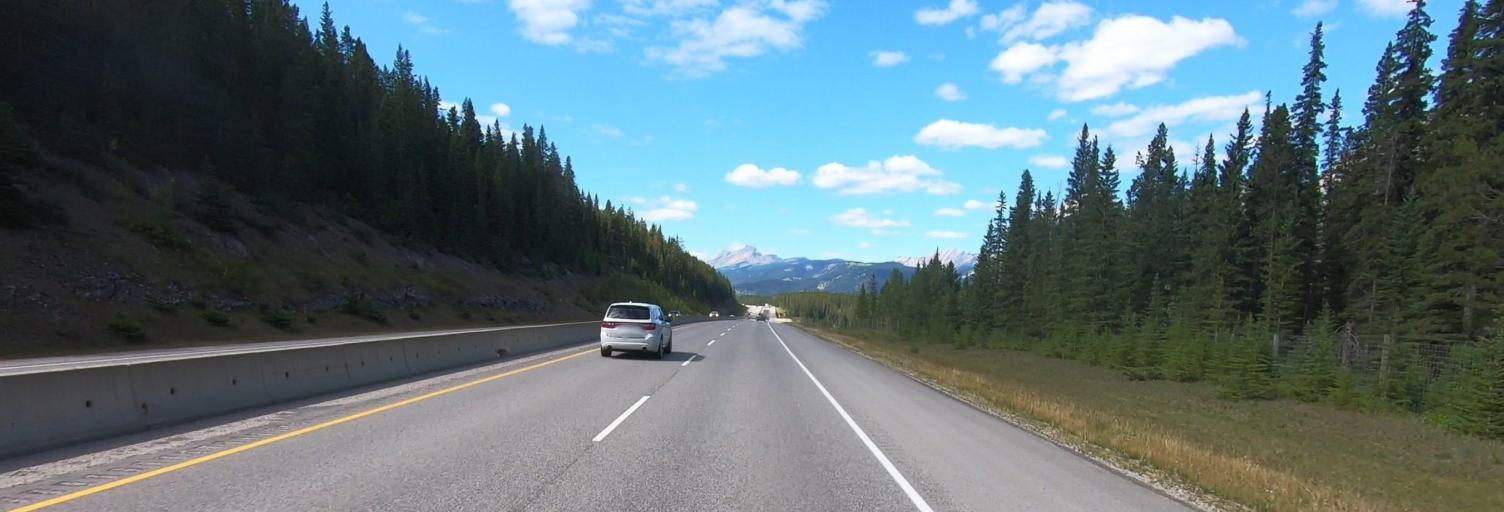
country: CA
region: Alberta
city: Banff
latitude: 51.1785
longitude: -115.7416
